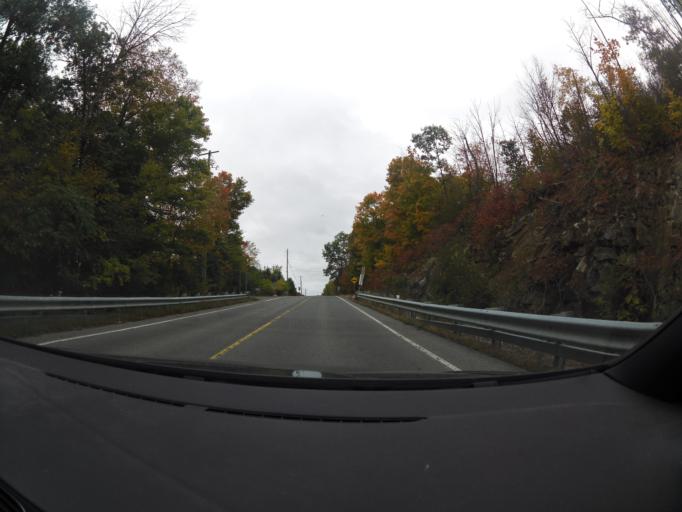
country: CA
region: Ontario
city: Bells Corners
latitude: 45.3300
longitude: -75.9715
